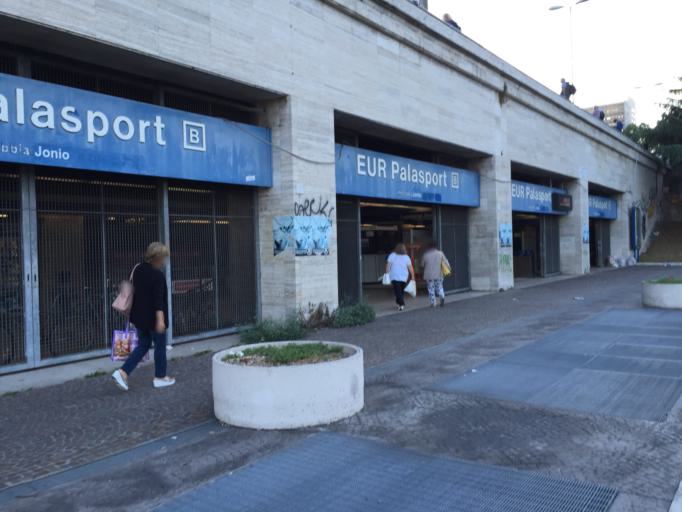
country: IT
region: Latium
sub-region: Citta metropolitana di Roma Capitale
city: Selcetta
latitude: 41.8299
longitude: 12.4664
